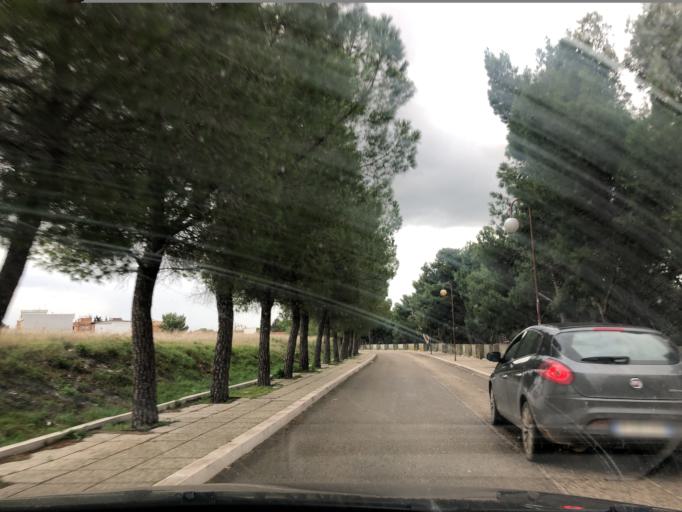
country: IT
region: Apulia
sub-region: Provincia di Foggia
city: Lucera
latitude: 41.5076
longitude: 15.3235
